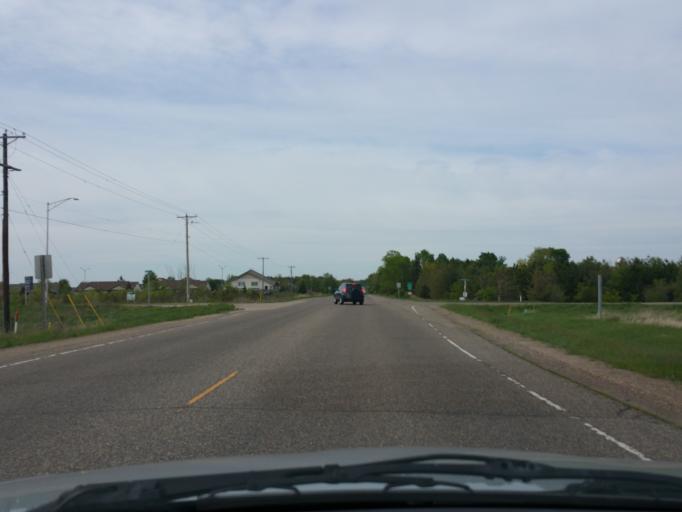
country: US
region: Wisconsin
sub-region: Saint Croix County
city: Hudson
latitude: 44.9482
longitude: -92.6906
